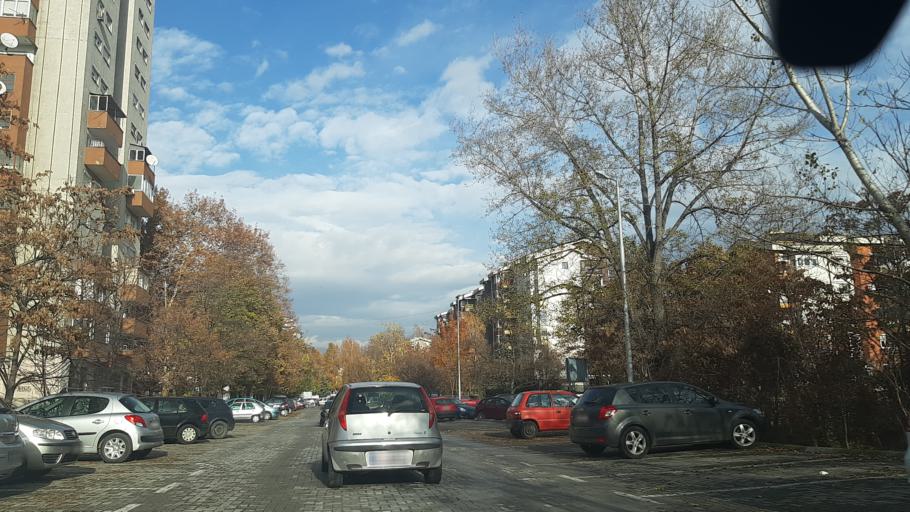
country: MK
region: Kisela Voda
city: Usje
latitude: 41.9827
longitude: 21.4641
